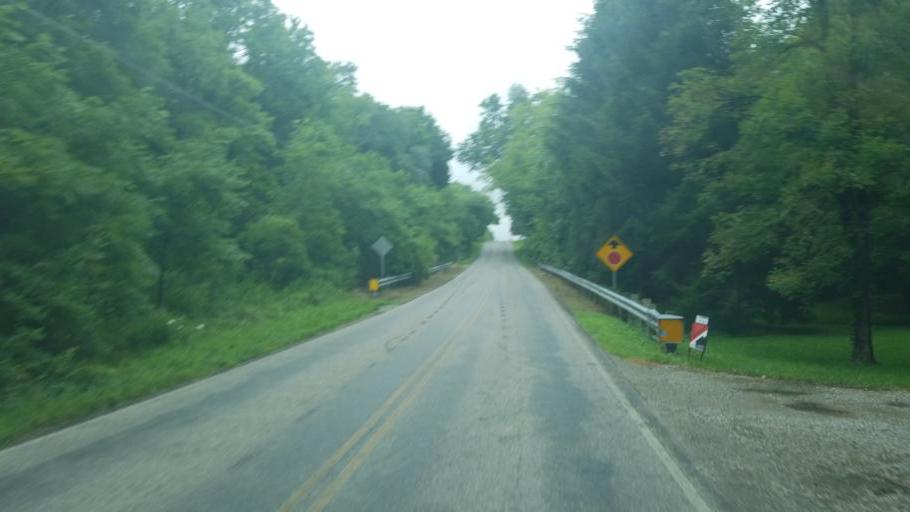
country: US
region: Ohio
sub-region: Delaware County
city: Sunbury
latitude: 40.2944
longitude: -82.8757
